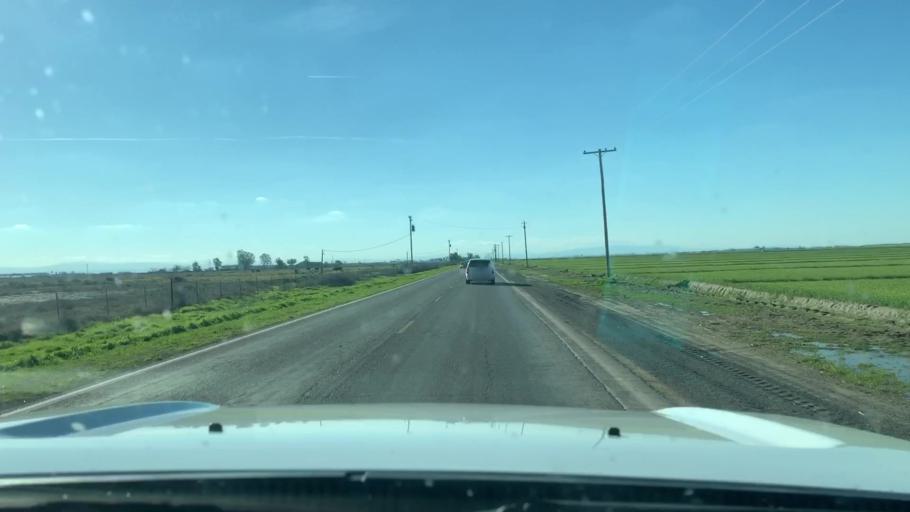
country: US
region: California
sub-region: Kings County
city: Home Garden
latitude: 36.2112
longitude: -119.6655
